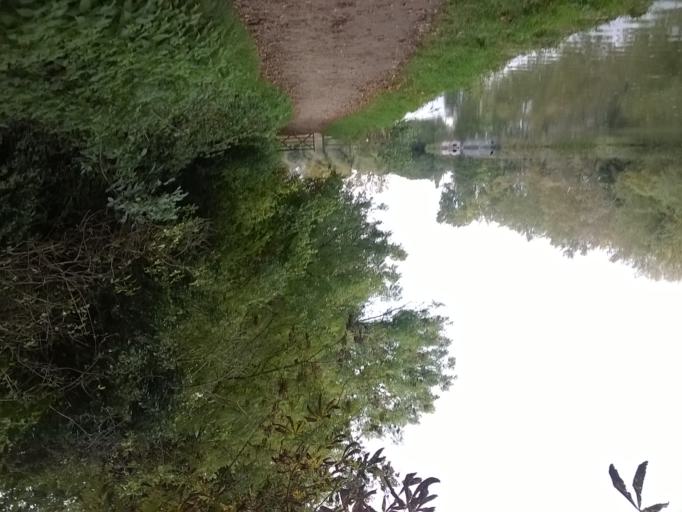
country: GB
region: England
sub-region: Wokingham
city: Sonning
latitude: 51.4697
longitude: -0.9207
